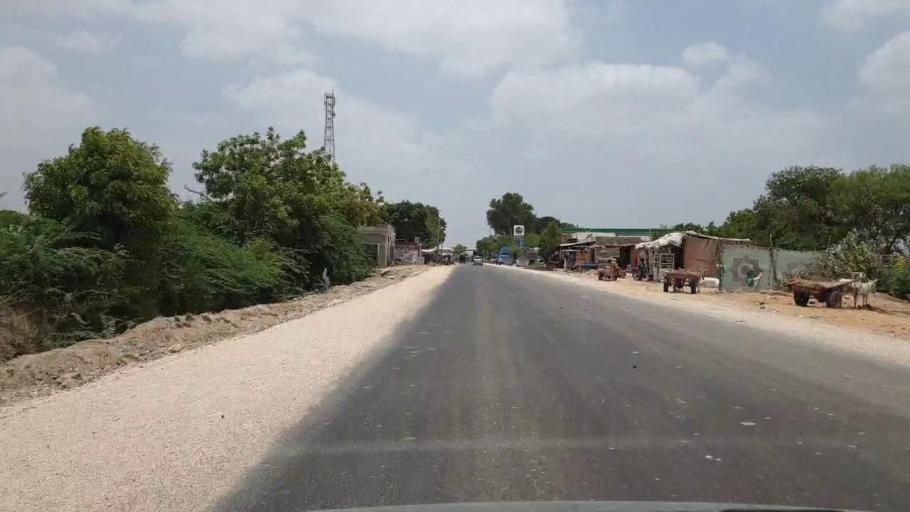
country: PK
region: Sindh
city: Naukot
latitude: 24.8462
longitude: 69.4182
